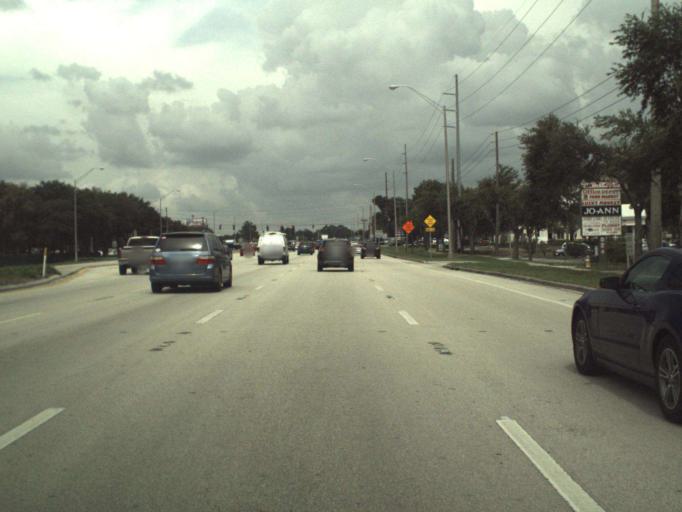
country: US
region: Florida
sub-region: Seminole County
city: Forest City
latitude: 28.6652
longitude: -81.4218
